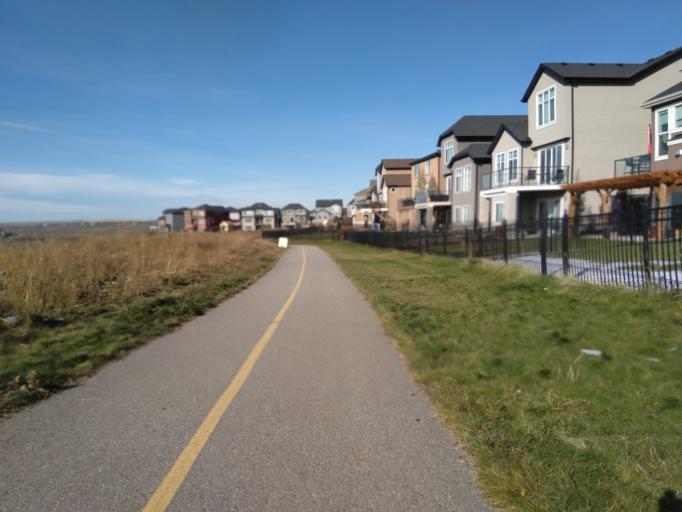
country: CA
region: Alberta
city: Calgary
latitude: 51.1745
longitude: -114.1236
